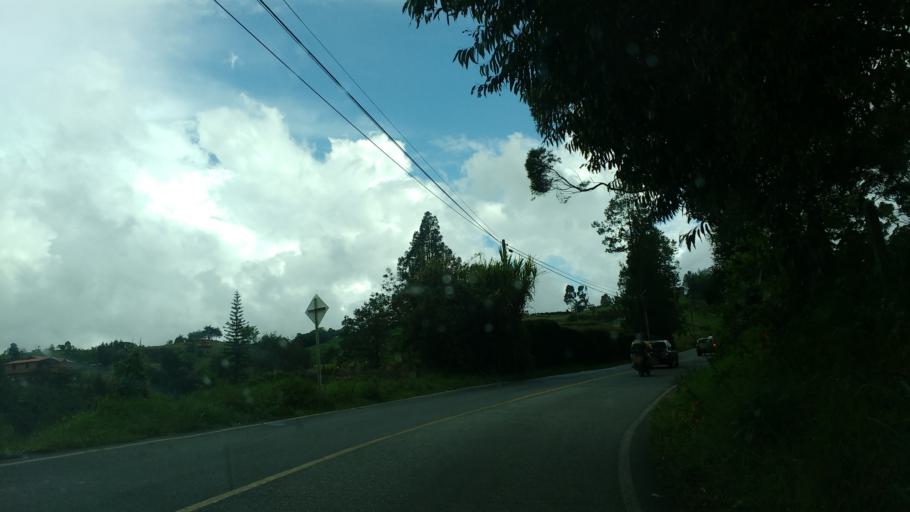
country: CO
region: Antioquia
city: Marinilla
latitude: 6.1993
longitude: -75.2846
